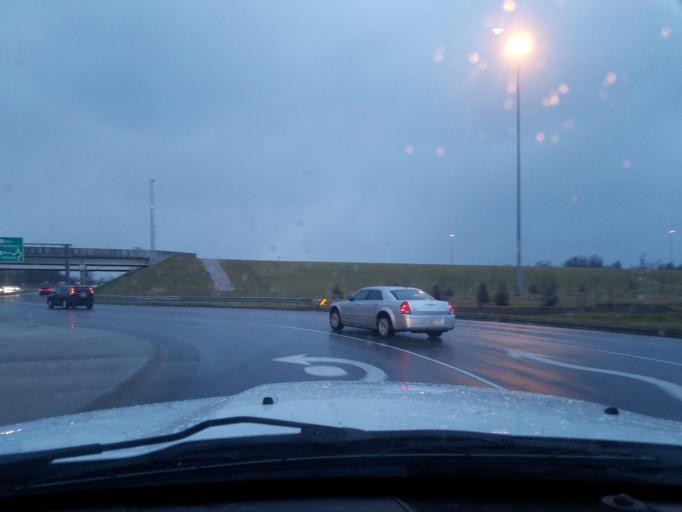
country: US
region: Indiana
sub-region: Clark County
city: Oak Park
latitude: 38.3429
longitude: -85.7060
